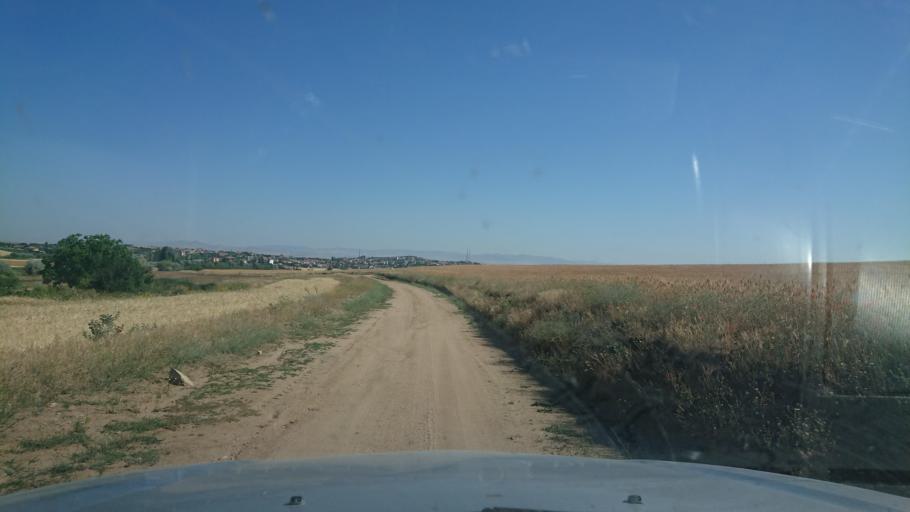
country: TR
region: Aksaray
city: Agacoren
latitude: 38.8532
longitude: 33.9146
